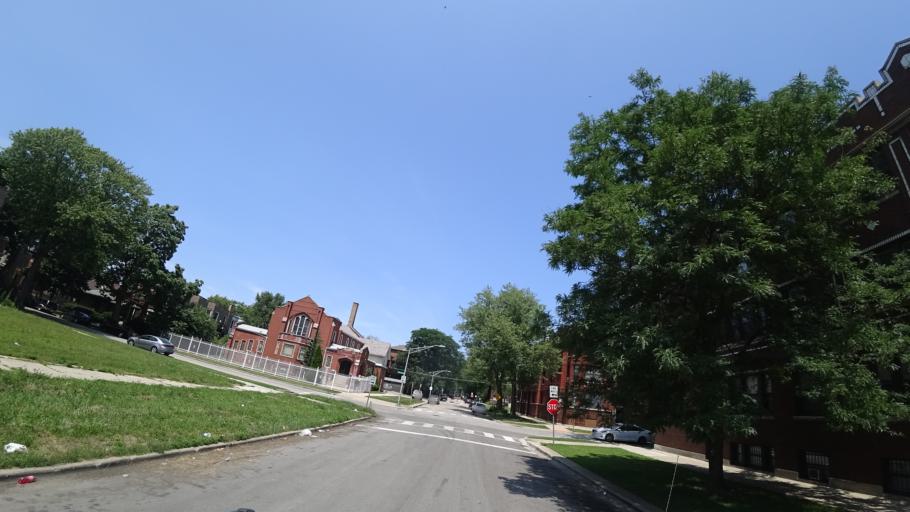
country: US
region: Illinois
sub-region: Cook County
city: Chicago
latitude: 41.7685
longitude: -87.5879
